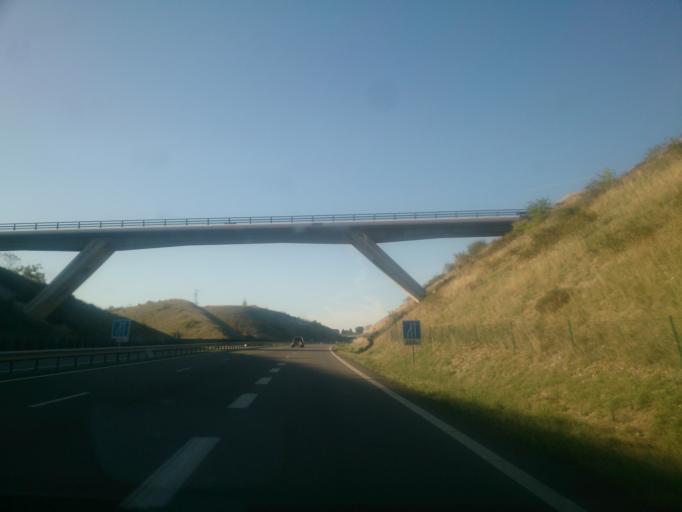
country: FR
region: Midi-Pyrenees
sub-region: Departement du Lot
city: Cahors
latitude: 44.4907
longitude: 1.4952
